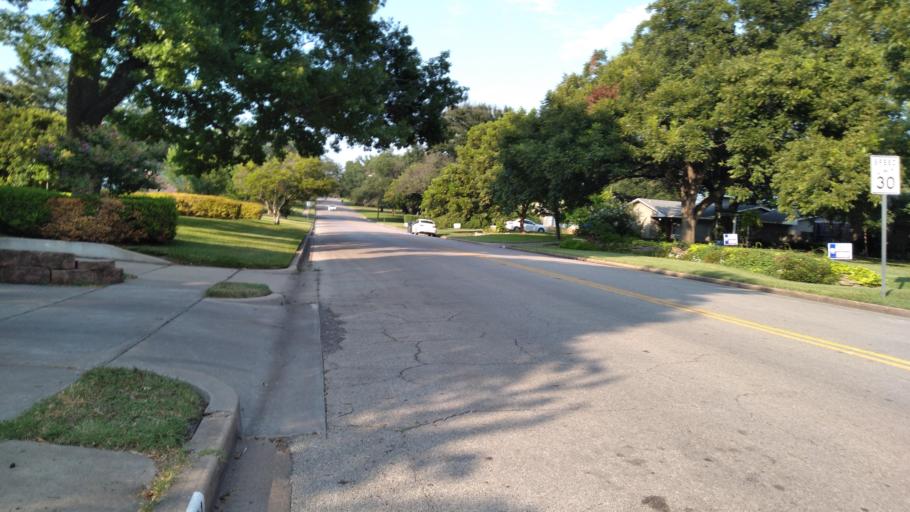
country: US
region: Texas
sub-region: McLennan County
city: Beverly Hills
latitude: 31.5313
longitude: -97.1608
